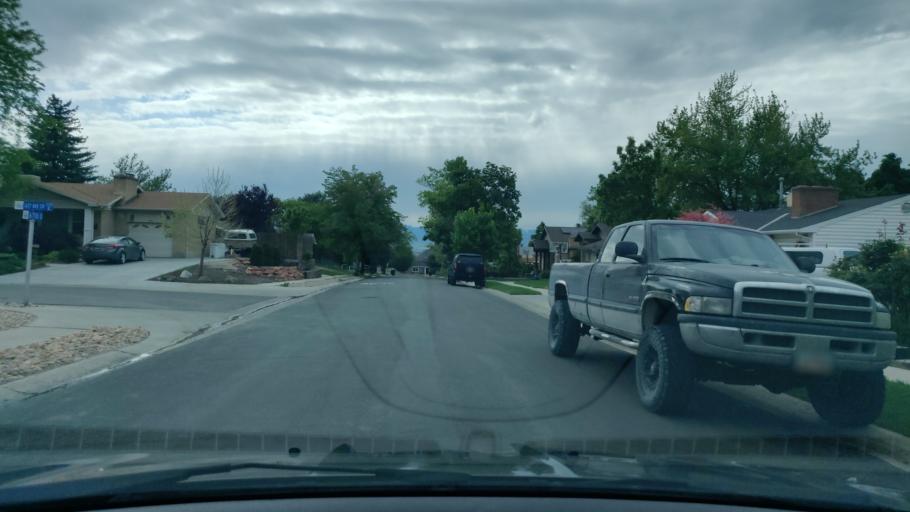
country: US
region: Utah
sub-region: Salt Lake County
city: Cottonwood Heights
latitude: 40.6292
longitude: -111.8223
